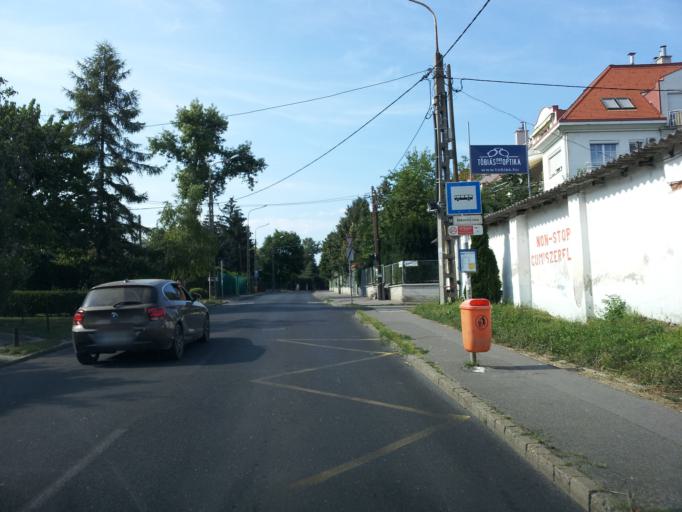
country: HU
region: Budapest
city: Budapest III. keruelet
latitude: 47.5320
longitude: 19.0291
